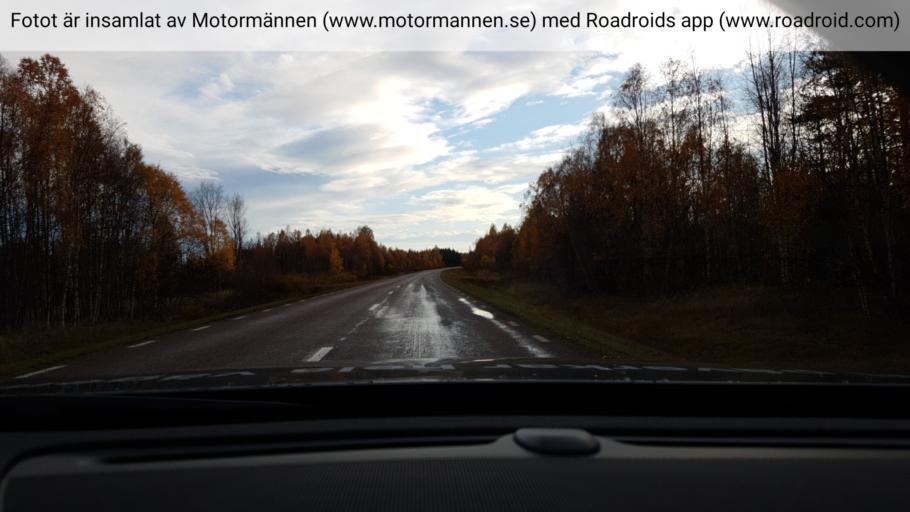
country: SE
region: Norrbotten
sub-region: Pajala Kommun
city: Pajala
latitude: 67.1526
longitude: 22.6285
